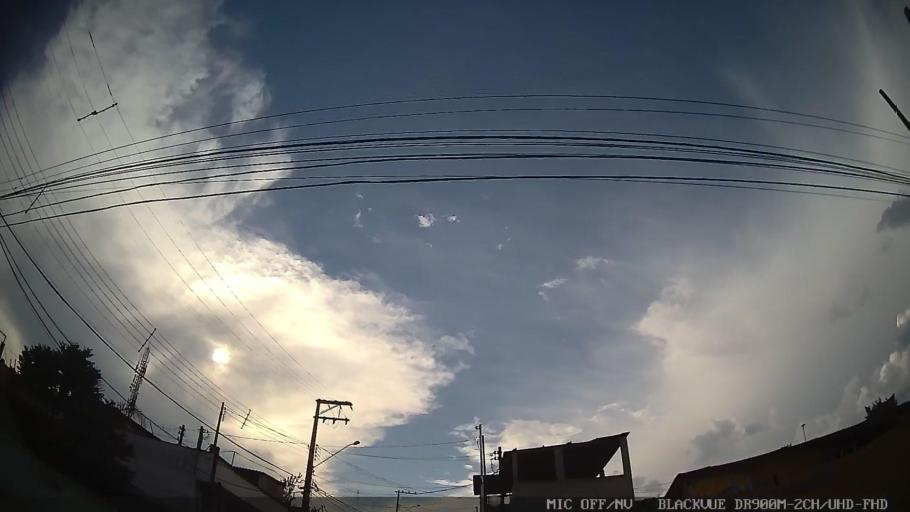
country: BR
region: Sao Paulo
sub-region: Braganca Paulista
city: Braganca Paulista
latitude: -22.9166
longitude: -46.5507
